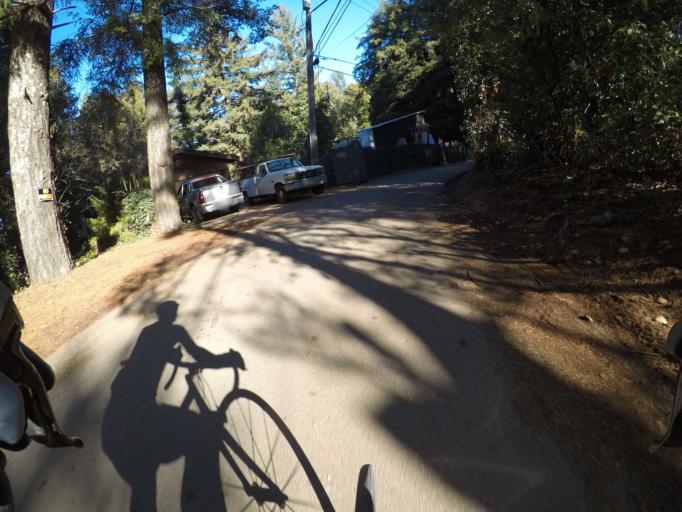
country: US
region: California
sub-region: Santa Cruz County
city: Mount Hermon
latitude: 37.0484
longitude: -122.0606
